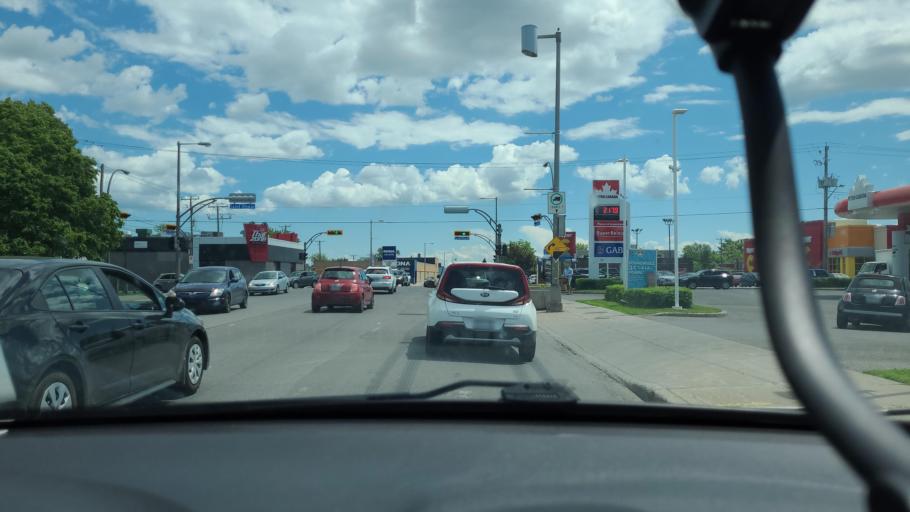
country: CA
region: Quebec
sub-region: Laval
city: Laval
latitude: 45.6035
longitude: -73.7291
